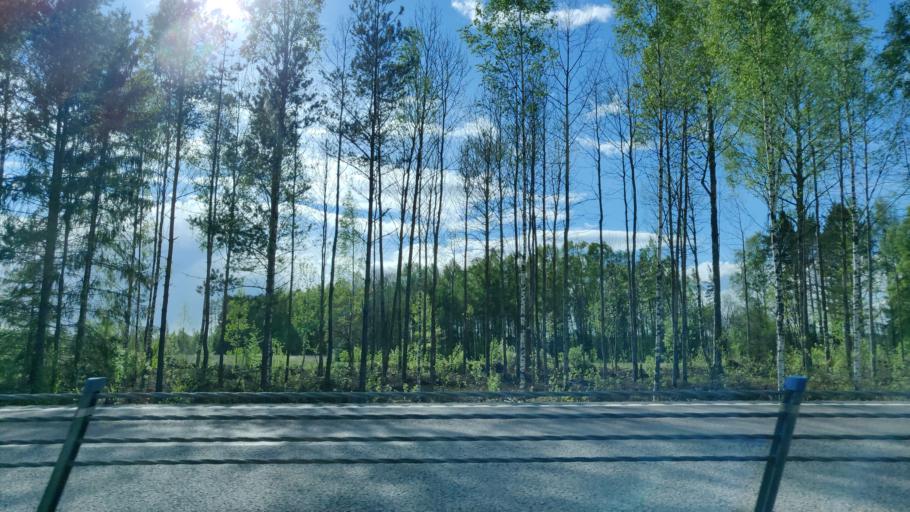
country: SE
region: Vaermland
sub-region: Forshaga Kommun
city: Forshaga
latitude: 59.4748
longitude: 13.4107
